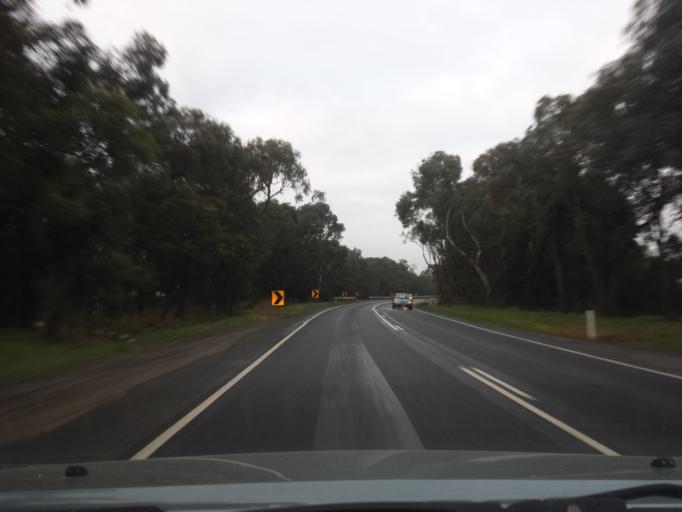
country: AU
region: Victoria
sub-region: Yarra Ranges
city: Belgrave South
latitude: -37.9612
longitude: 145.3443
